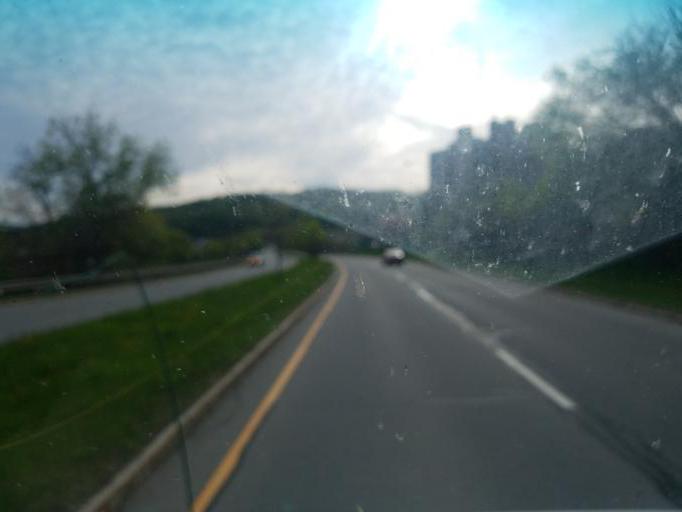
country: US
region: New York
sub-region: Herkimer County
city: Little Falls
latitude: 43.0425
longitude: -74.8552
